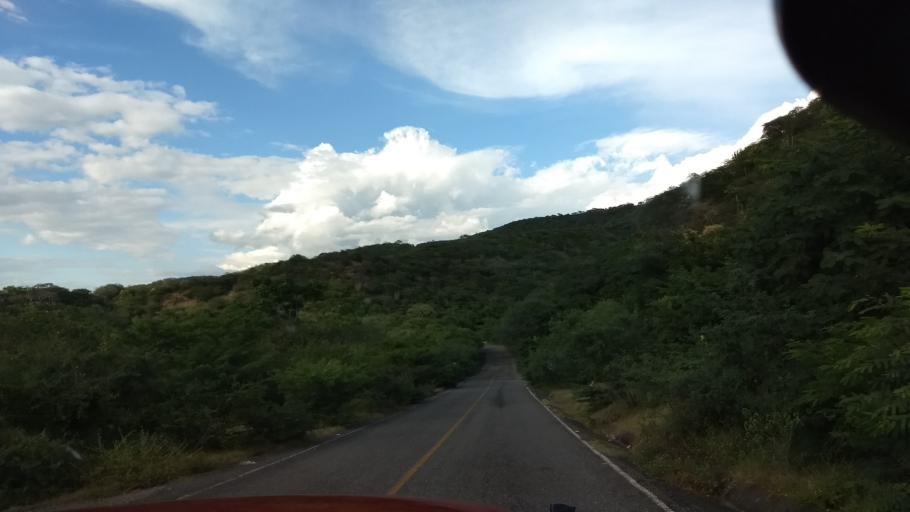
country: MX
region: Colima
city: Suchitlan
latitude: 19.4610
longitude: -103.8253
